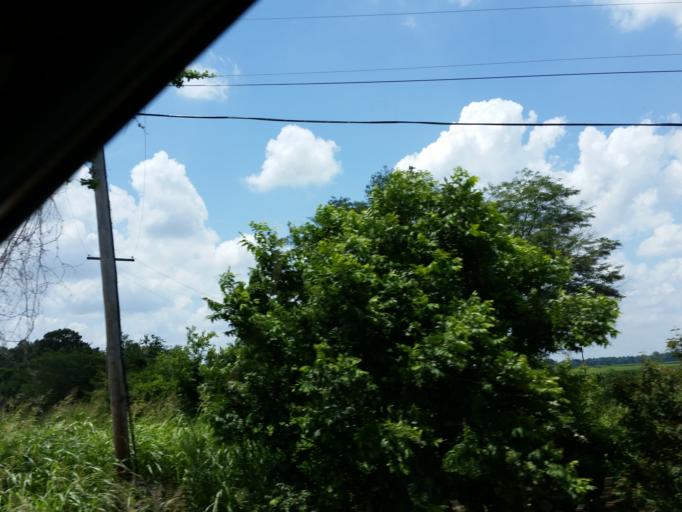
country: US
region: Tennessee
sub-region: Lake County
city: Ridgely
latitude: 36.1983
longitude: -89.4572
